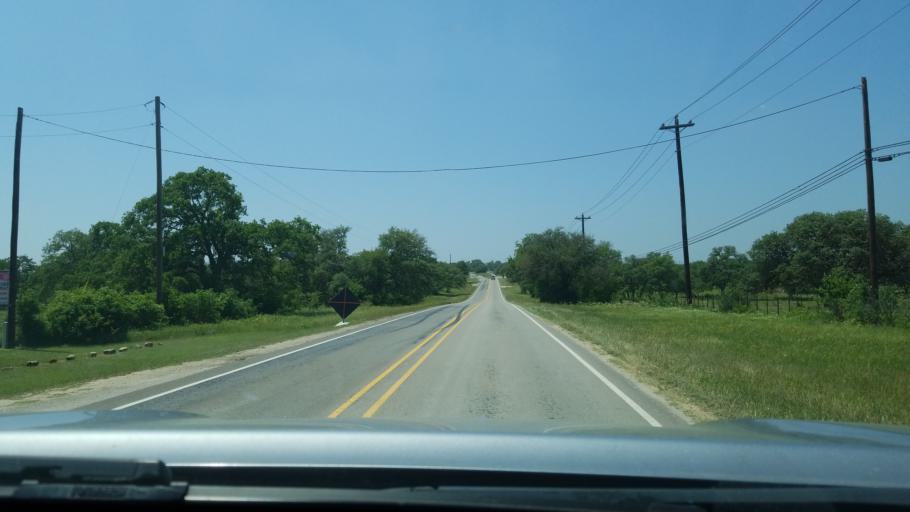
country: US
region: Texas
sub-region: Blanco County
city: Blanco
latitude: 30.0688
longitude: -98.4028
